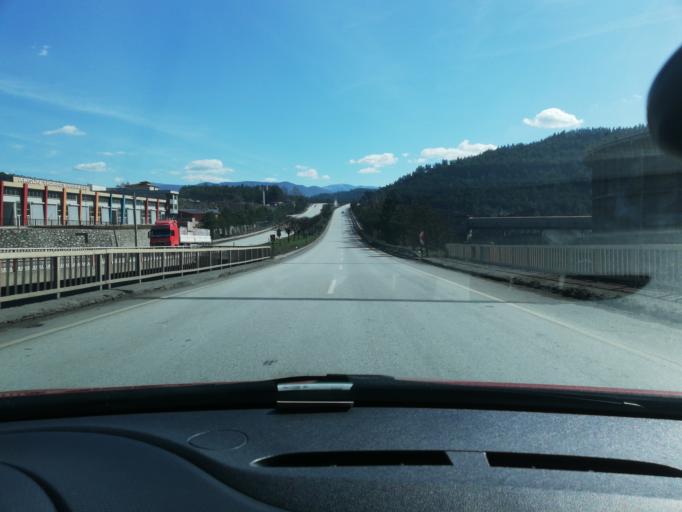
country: TR
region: Karabuk
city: Karabuk
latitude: 41.1695
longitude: 32.6370
